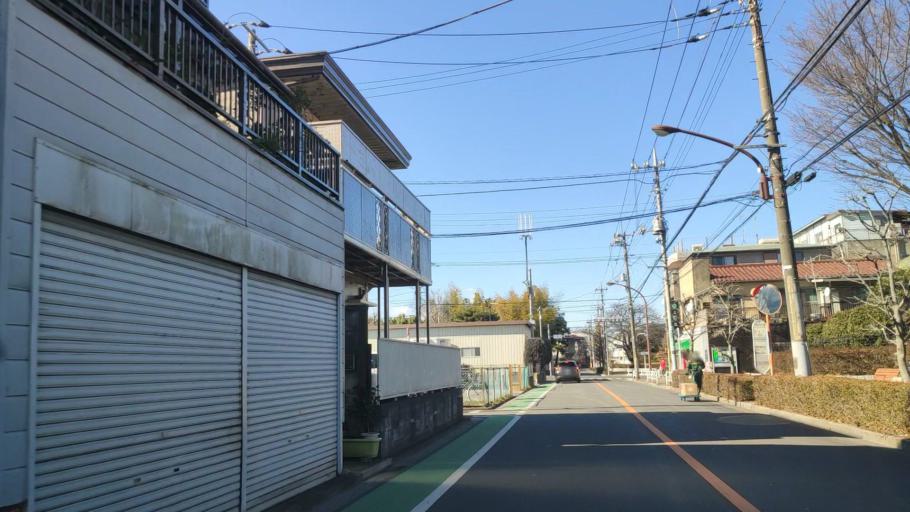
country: JP
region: Tokyo
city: Musashino
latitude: 35.7176
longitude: 139.5564
